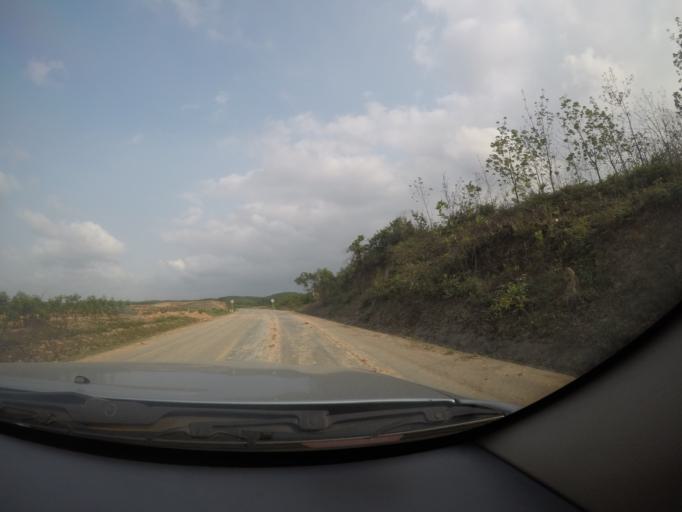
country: VN
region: Quang Binh
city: Kien Giang
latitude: 17.0969
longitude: 106.8483
